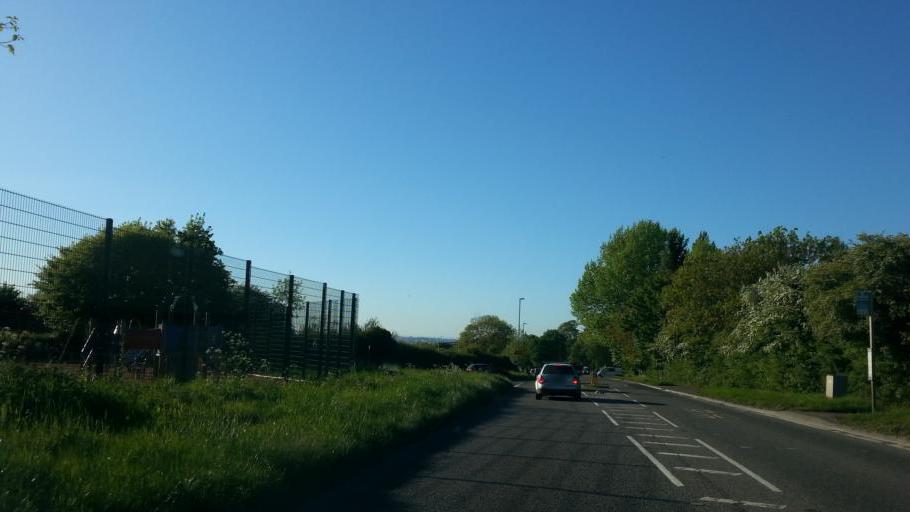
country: GB
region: England
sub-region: Bath and North East Somerset
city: Whitchurch
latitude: 51.4002
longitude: -2.5520
